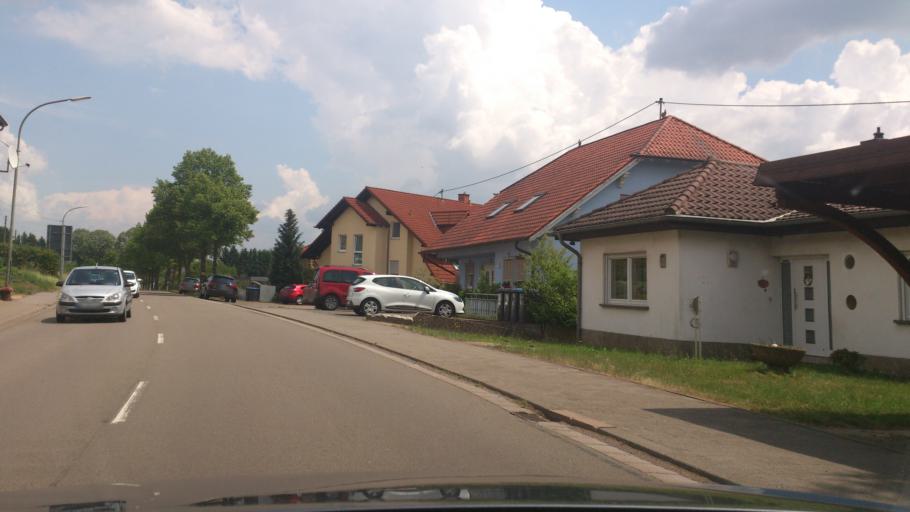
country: DE
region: Saarland
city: Illingen
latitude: 49.3803
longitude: 7.0343
